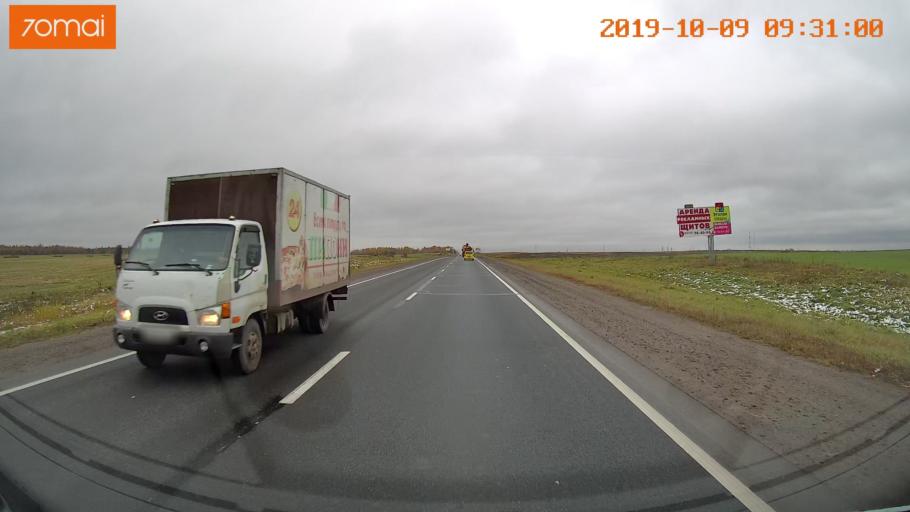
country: RU
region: Vologda
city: Vologda
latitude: 59.1454
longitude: 39.9432
